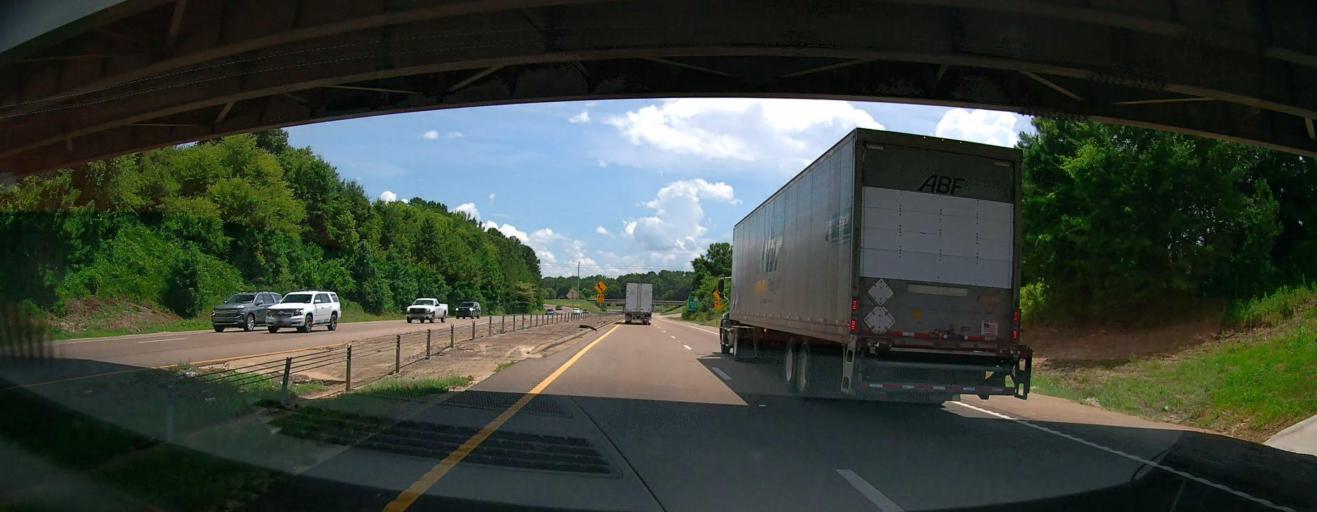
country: US
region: Mississippi
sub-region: Lee County
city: Tupelo
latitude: 34.2798
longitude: -88.7076
